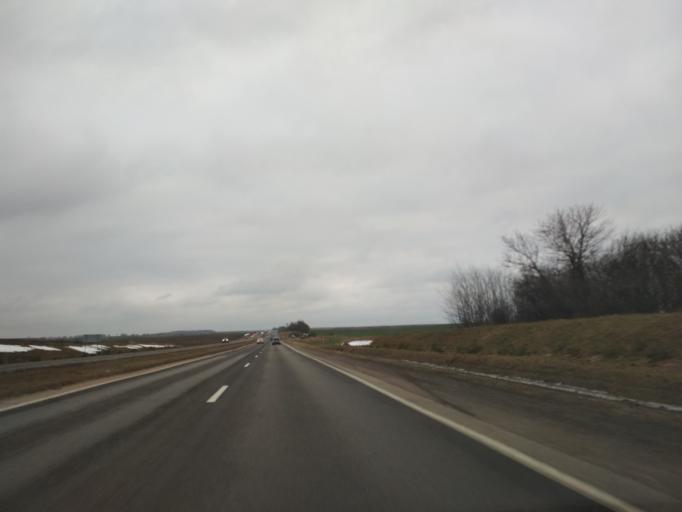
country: BY
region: Minsk
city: Blon'
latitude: 53.5699
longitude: 28.1360
